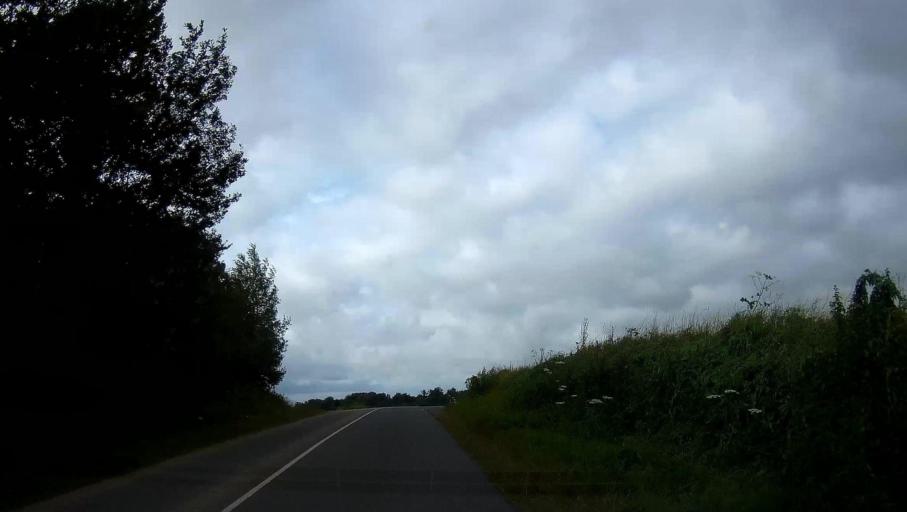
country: FR
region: Champagne-Ardenne
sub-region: Departement des Ardennes
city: Chateau-Porcien
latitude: 49.6229
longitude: 4.2346
